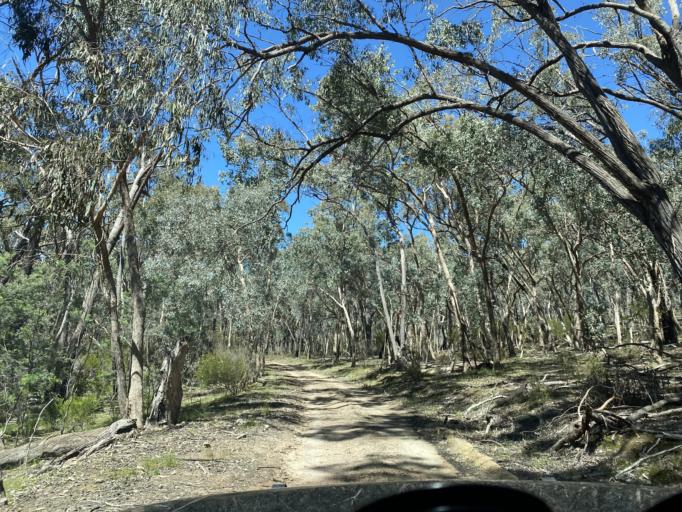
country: AU
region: Victoria
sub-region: Benalla
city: Benalla
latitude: -36.7012
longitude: 146.1516
